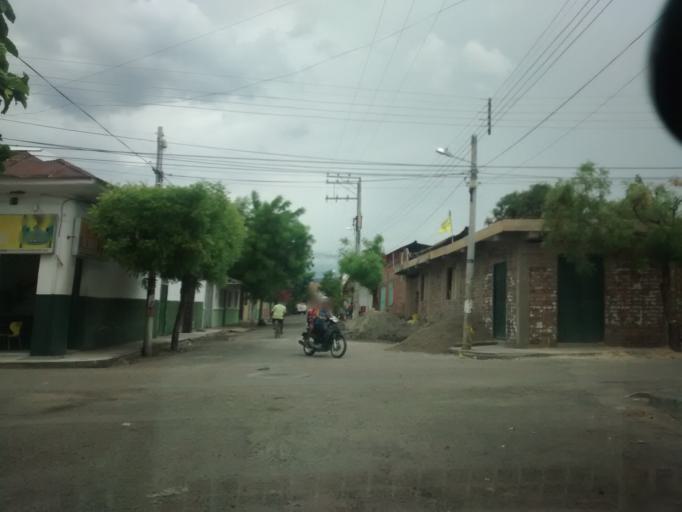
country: CO
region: Cundinamarca
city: Tocaima
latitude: 4.4592
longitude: -74.6335
